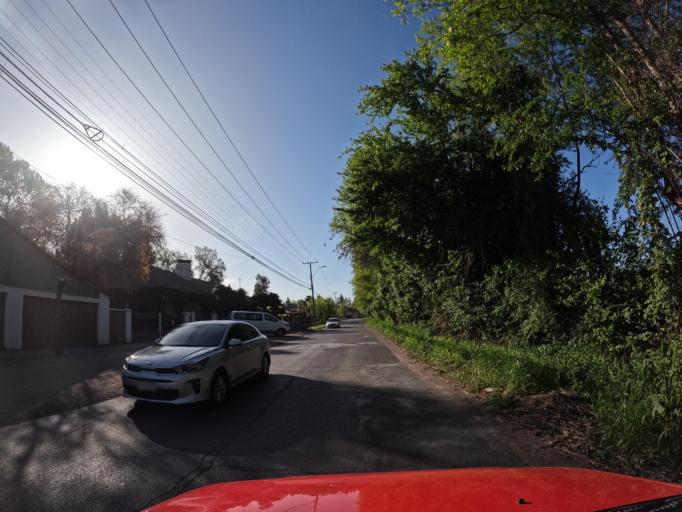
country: CL
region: O'Higgins
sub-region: Provincia de Colchagua
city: Santa Cruz
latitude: -34.7190
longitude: -71.2869
